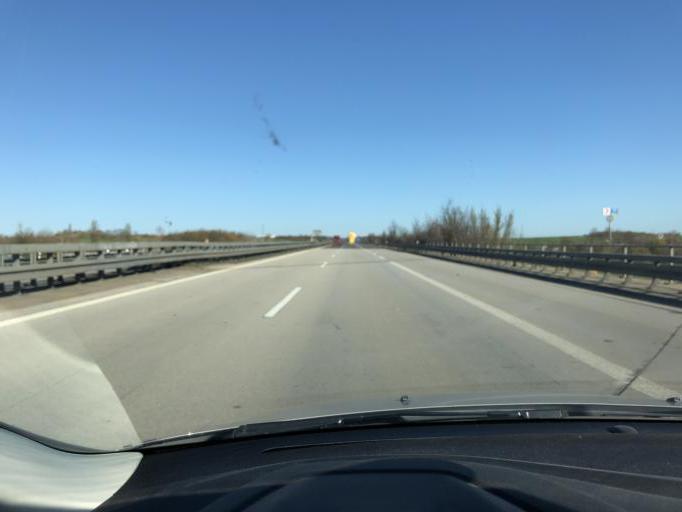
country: DE
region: Saxony-Anhalt
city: Oppin
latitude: 51.5412
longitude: 12.0130
